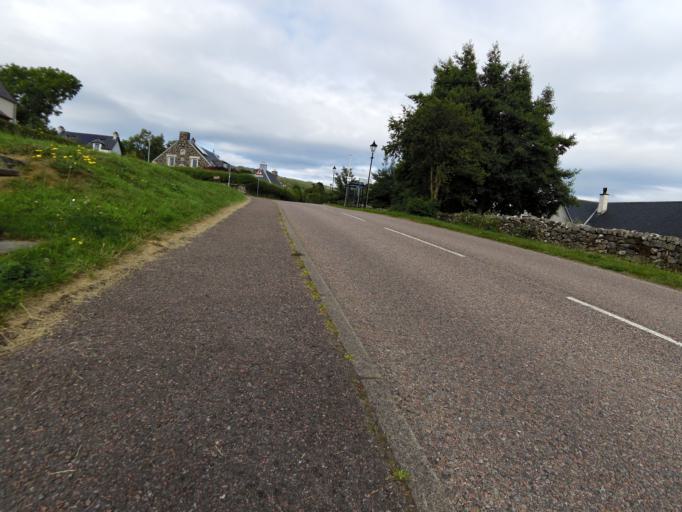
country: GB
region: Scotland
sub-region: Argyll and Bute
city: Isle Of Mull
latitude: 56.9099
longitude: -5.8432
